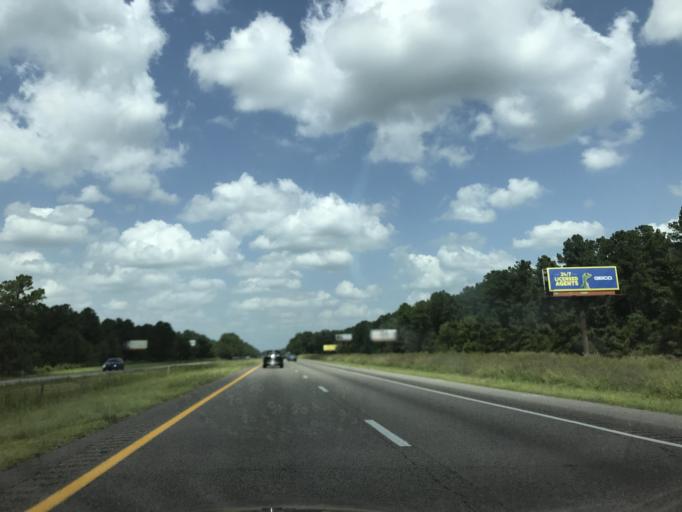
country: US
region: North Carolina
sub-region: Pender County
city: Burgaw
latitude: 34.6489
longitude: -77.9404
